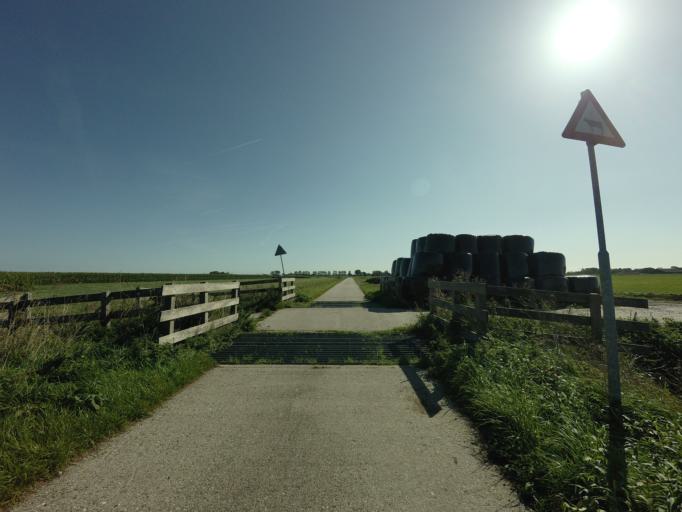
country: NL
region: Friesland
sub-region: Gemeente Leeuwarden
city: Wirdum
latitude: 53.1565
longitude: 5.7676
